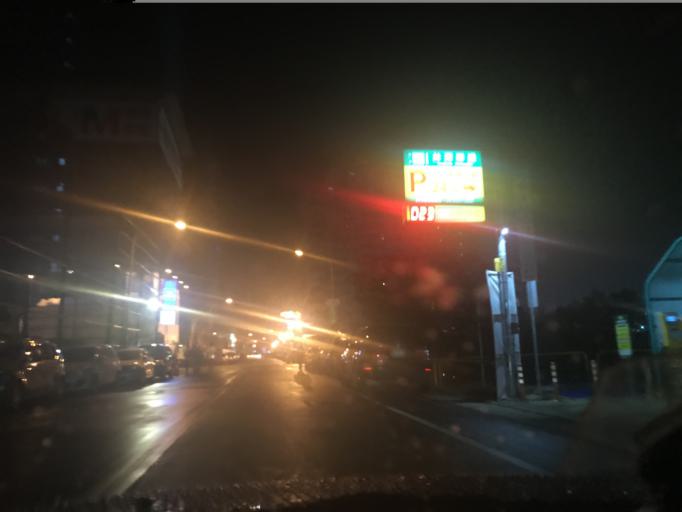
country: TW
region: Taiwan
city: Daxi
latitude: 24.9336
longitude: 121.2834
